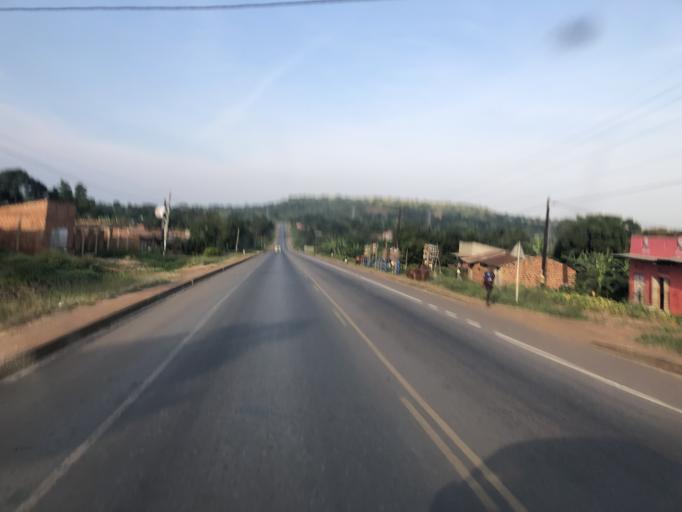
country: UG
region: Central Region
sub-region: Mpigi District
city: Mpigi
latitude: 0.1722
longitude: 32.2648
